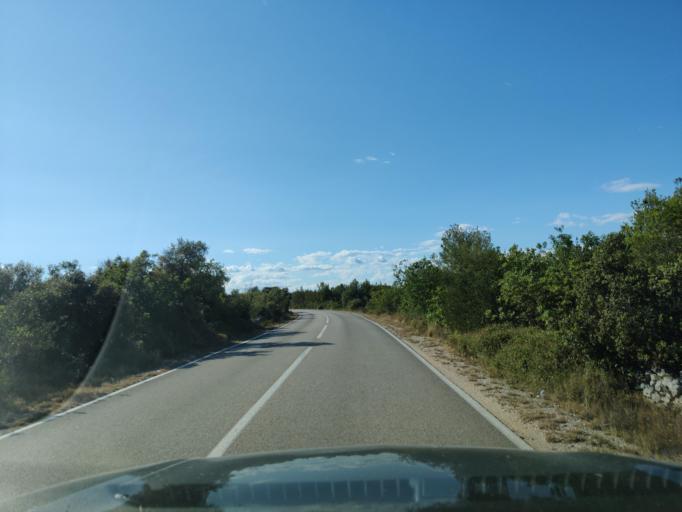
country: HR
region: Sibensko-Kniniska
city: Zaton
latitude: 43.7488
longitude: 15.8429
